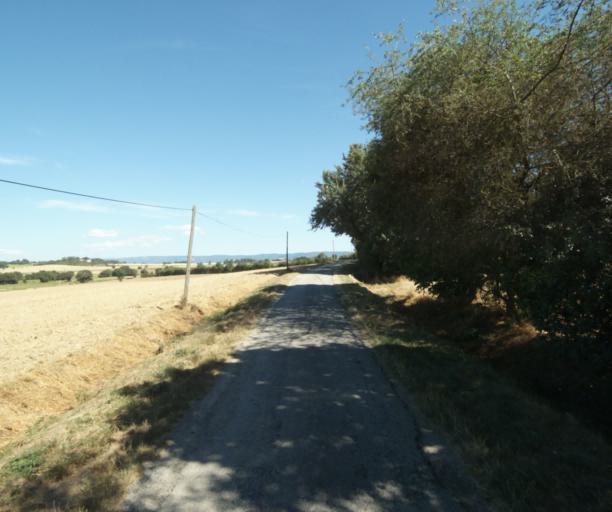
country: FR
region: Midi-Pyrenees
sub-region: Departement de la Haute-Garonne
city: Saint-Felix-Lauragais
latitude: 43.4965
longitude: 1.9027
